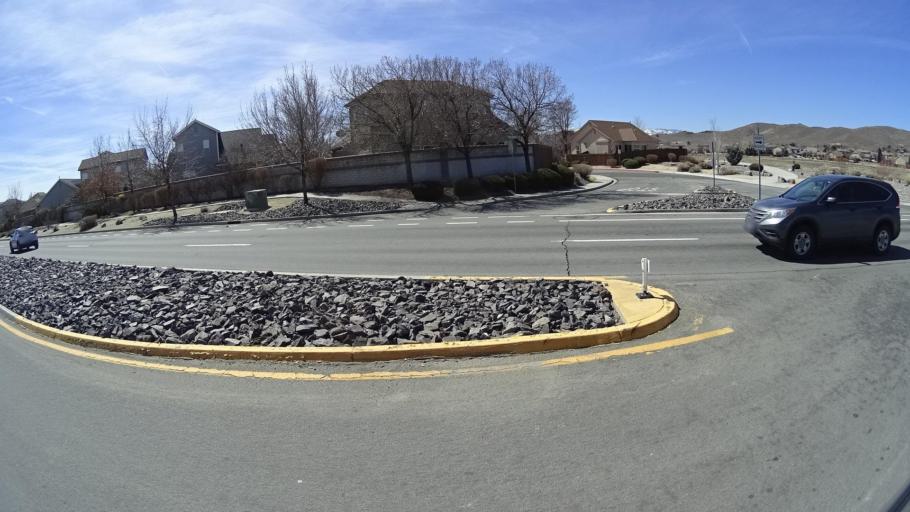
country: US
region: Nevada
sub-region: Washoe County
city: Sun Valley
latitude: 39.5896
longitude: -119.7281
